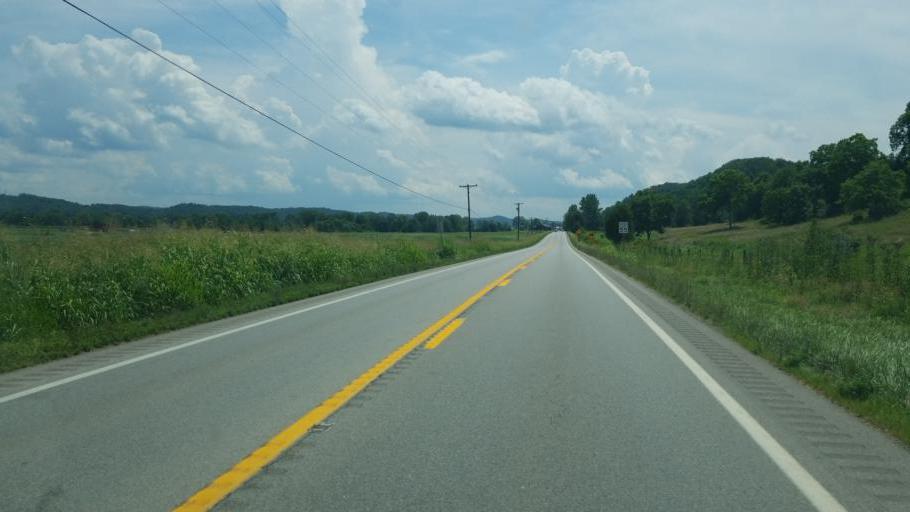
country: US
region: West Virginia
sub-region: Putnam County
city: Buffalo
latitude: 38.7265
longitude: -81.9719
